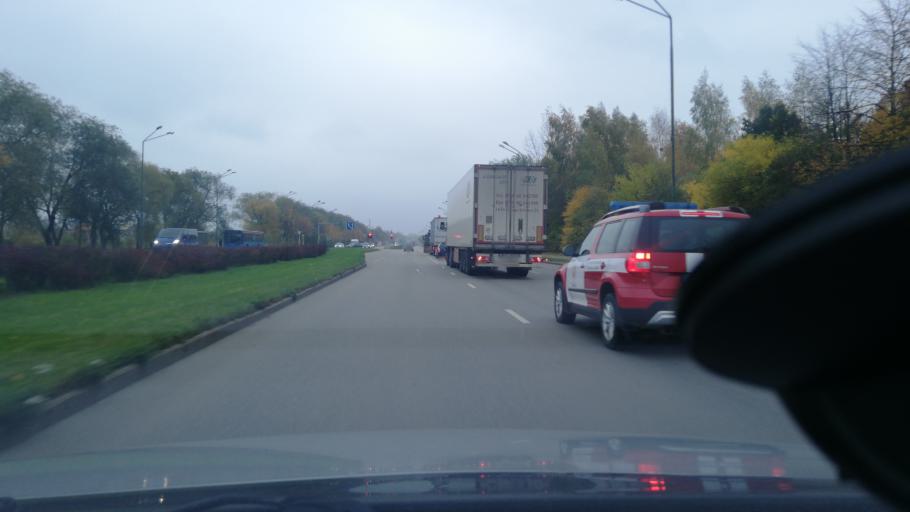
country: LT
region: Klaipedos apskritis
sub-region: Klaipeda
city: Klaipeda
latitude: 55.6762
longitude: 21.1913
